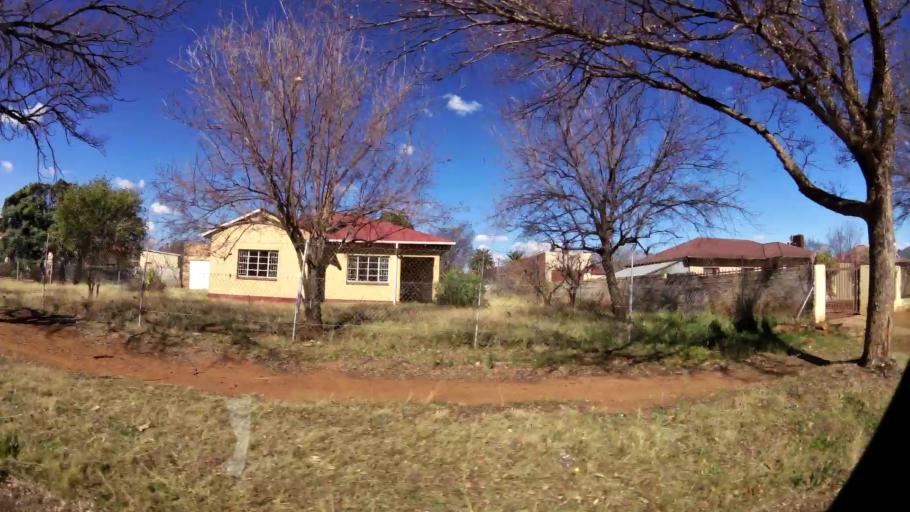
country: ZA
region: Gauteng
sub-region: West Rand District Municipality
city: Carletonville
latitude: -26.3637
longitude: 27.3905
